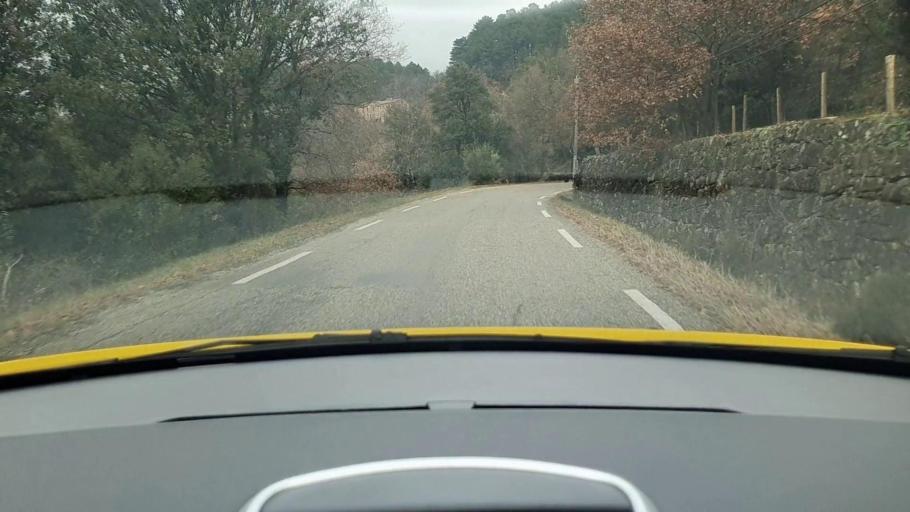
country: FR
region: Languedoc-Roussillon
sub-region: Departement du Gard
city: Besseges
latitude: 44.3134
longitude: 4.0747
